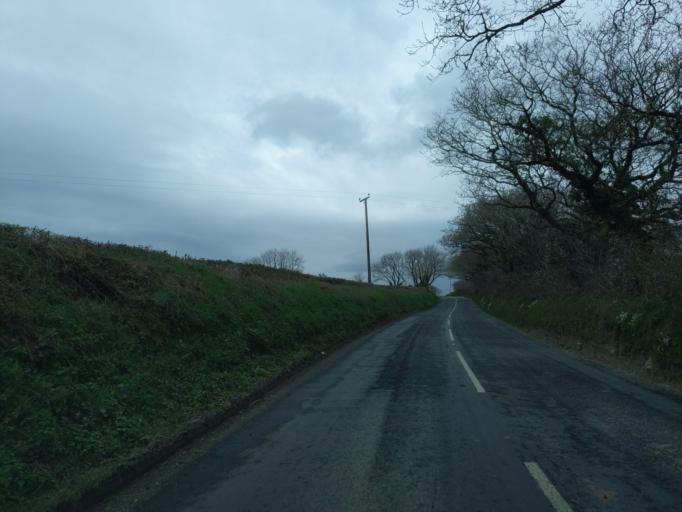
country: GB
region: England
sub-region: Cornwall
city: South Hill
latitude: 50.5468
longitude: -4.3659
